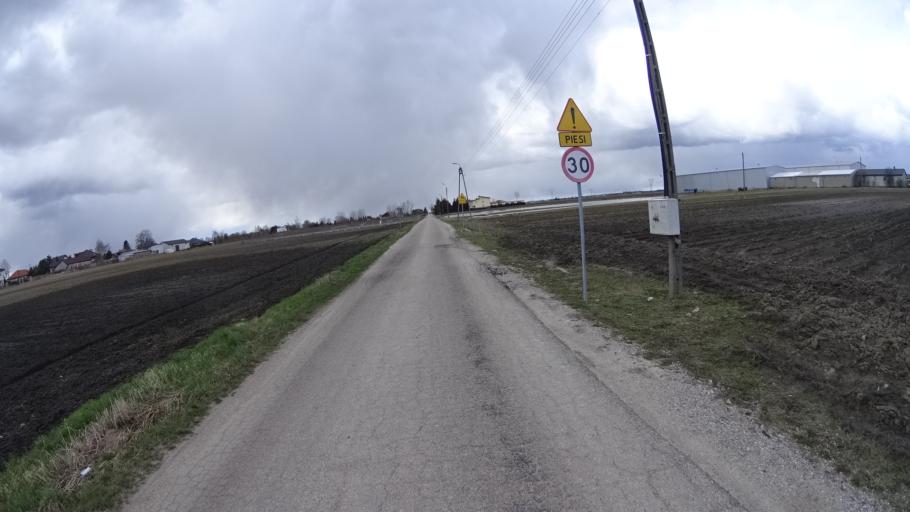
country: PL
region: Masovian Voivodeship
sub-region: Powiat warszawski zachodni
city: Jozefow
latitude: 52.2201
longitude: 20.6919
